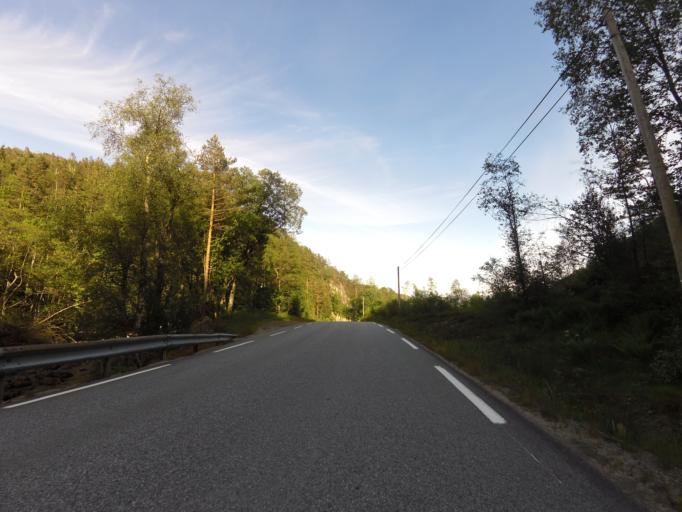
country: NO
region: Vest-Agder
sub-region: Flekkefjord
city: Flekkefjord
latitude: 58.2801
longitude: 6.6246
